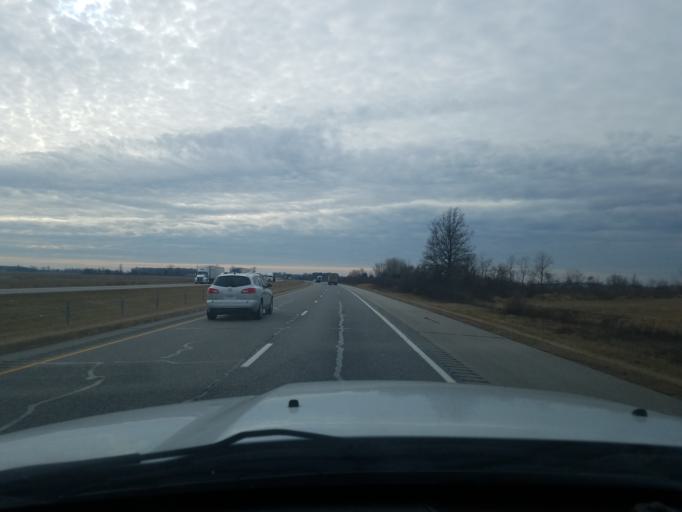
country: US
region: Indiana
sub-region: Huntington County
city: Warren
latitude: 40.6904
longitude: -85.4747
